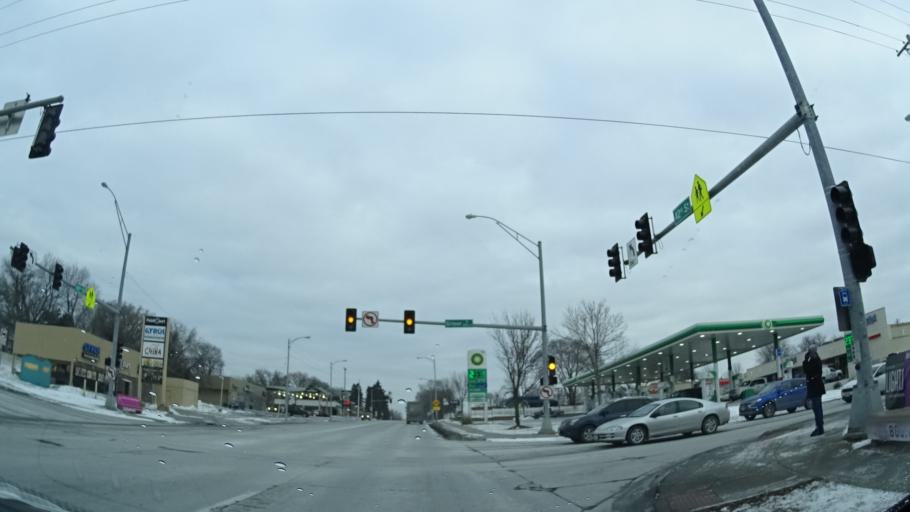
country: US
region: Nebraska
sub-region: Douglas County
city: Omaha
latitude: 41.2267
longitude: -95.9758
